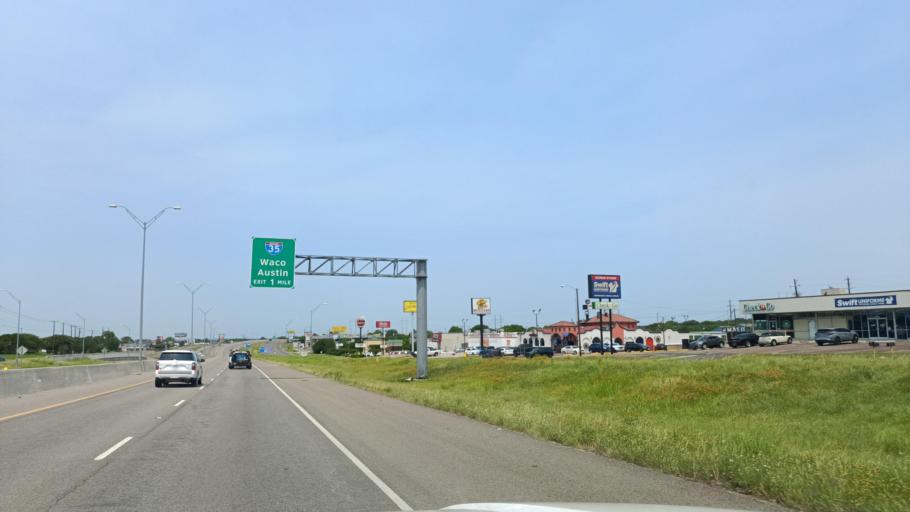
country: US
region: Texas
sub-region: Bell County
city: Temple
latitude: 31.0744
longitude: -97.3713
